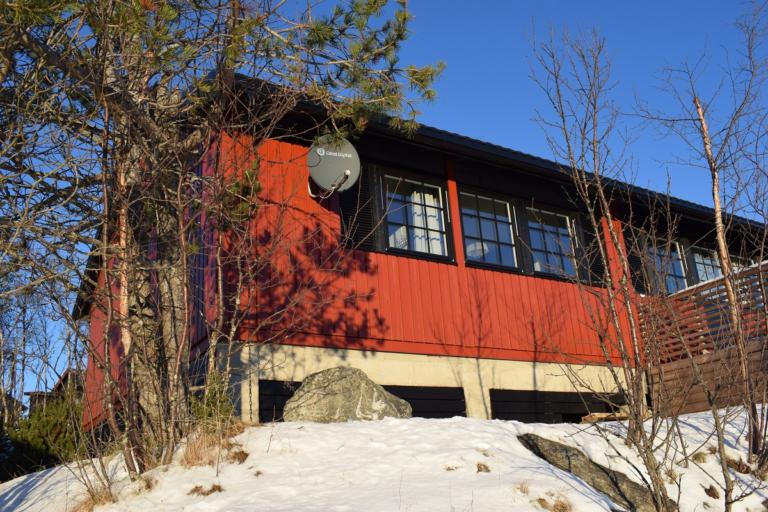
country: NO
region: Oppland
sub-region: Gausdal
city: Segalstad bru
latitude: 61.3123
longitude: 10.0694
